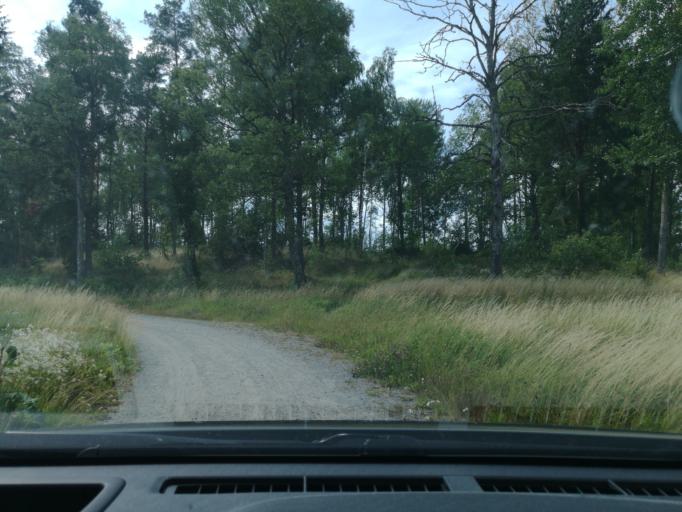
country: SE
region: Stockholm
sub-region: Sigtuna Kommun
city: Marsta
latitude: 59.6151
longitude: 17.8002
